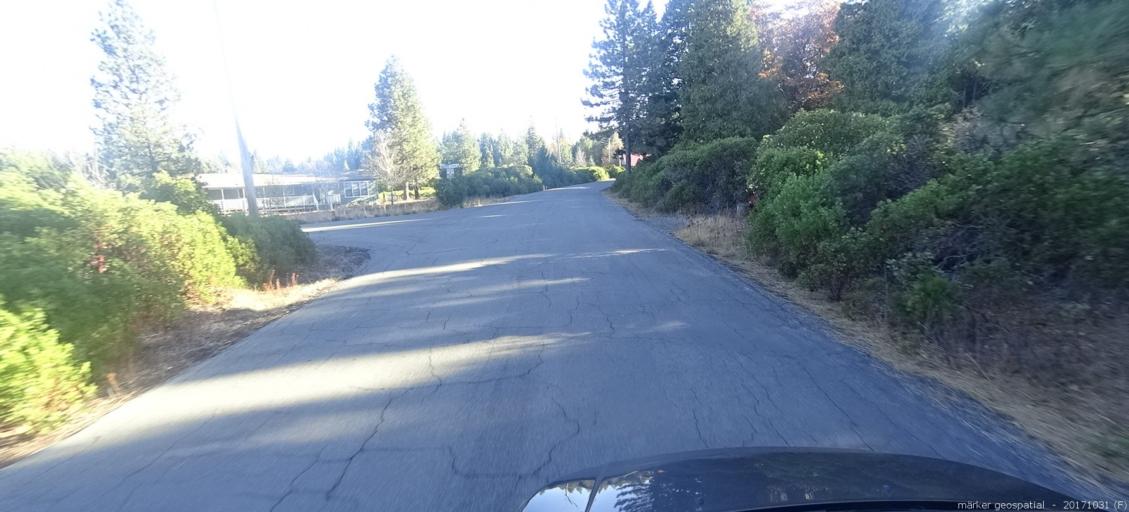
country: US
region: California
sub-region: Shasta County
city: Shingletown
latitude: 40.5219
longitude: -121.8389
